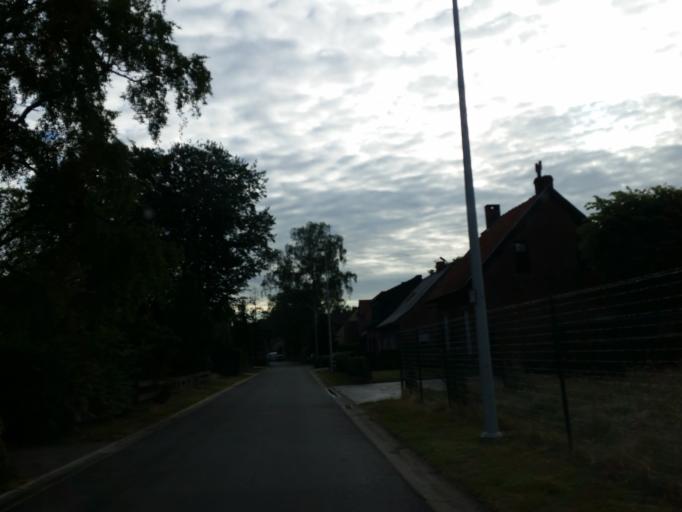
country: BE
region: Flanders
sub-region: Provincie Antwerpen
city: Kapellen
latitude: 51.3074
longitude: 4.4608
